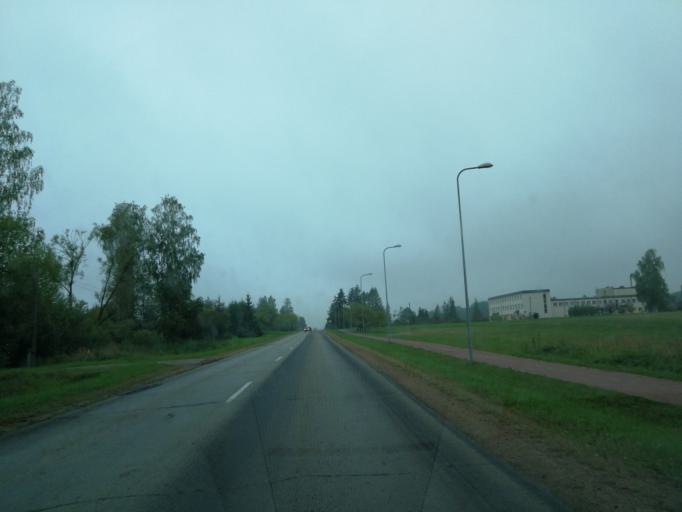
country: LV
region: Preilu Rajons
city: Preili
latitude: 56.2986
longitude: 26.6932
